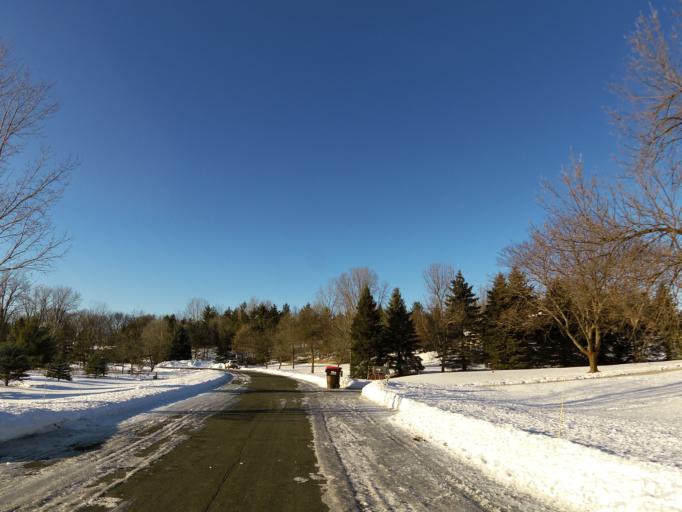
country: US
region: Minnesota
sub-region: Washington County
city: Lake Elmo
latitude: 44.9768
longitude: -92.8602
